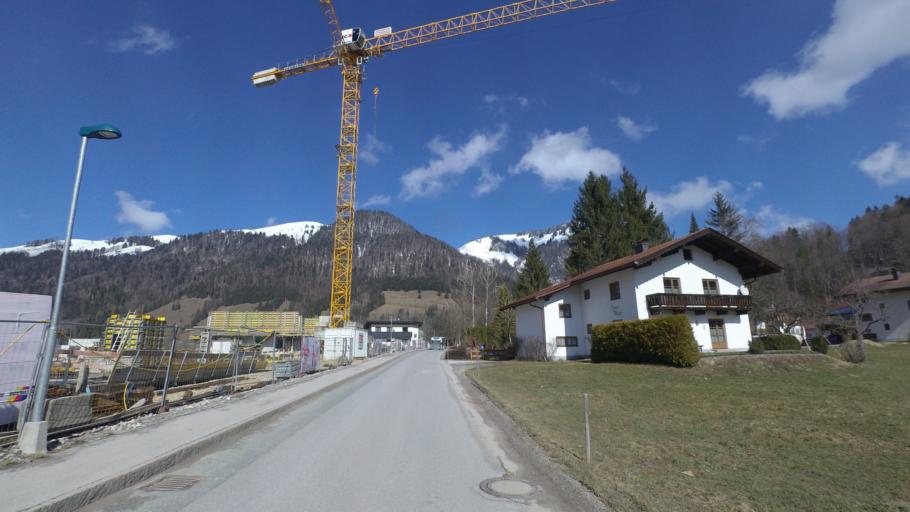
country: AT
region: Tyrol
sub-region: Politischer Bezirk Kufstein
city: Walchsee
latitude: 47.6554
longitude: 12.3184
